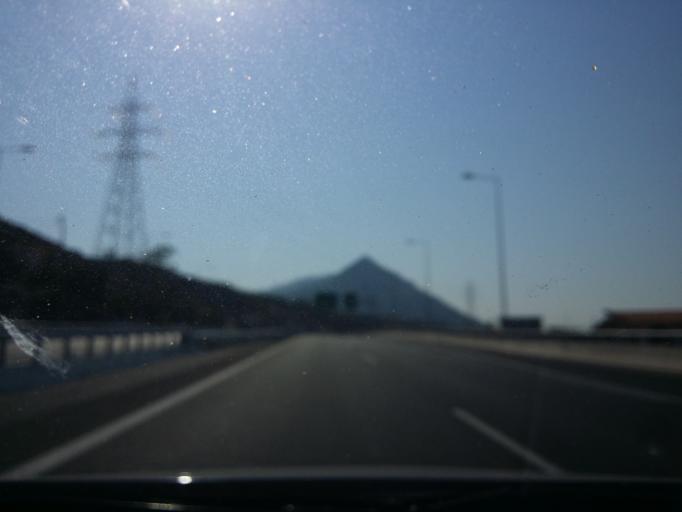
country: GR
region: Peloponnese
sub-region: Nomos Korinthias
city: Xylokastro
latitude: 38.0726
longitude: 22.6201
